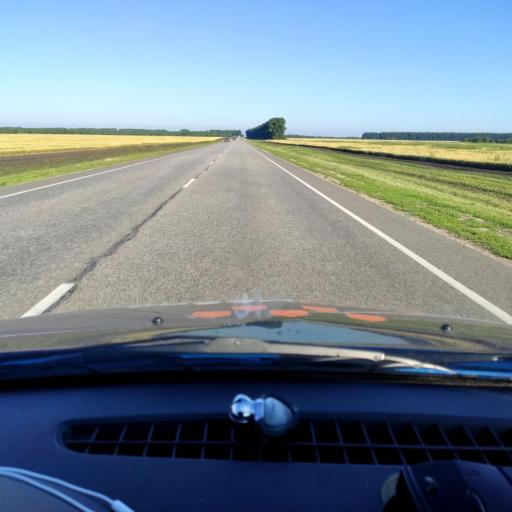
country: RU
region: Orjol
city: Pokrovskoye
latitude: 52.6338
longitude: 36.6932
